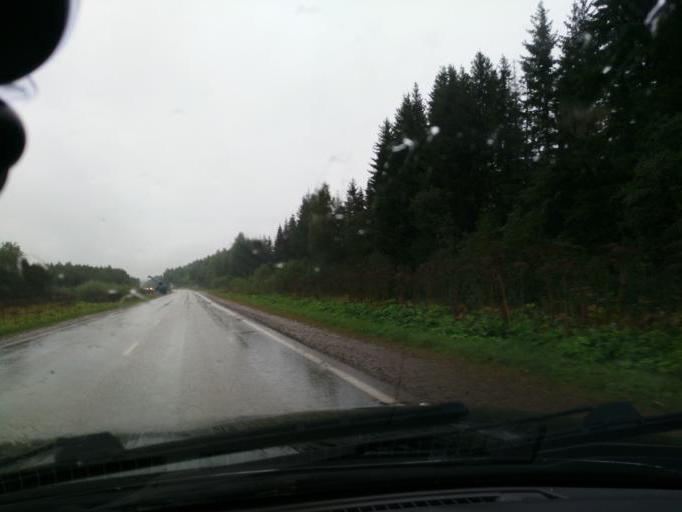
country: RU
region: Perm
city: Osa
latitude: 57.3518
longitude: 55.5963
